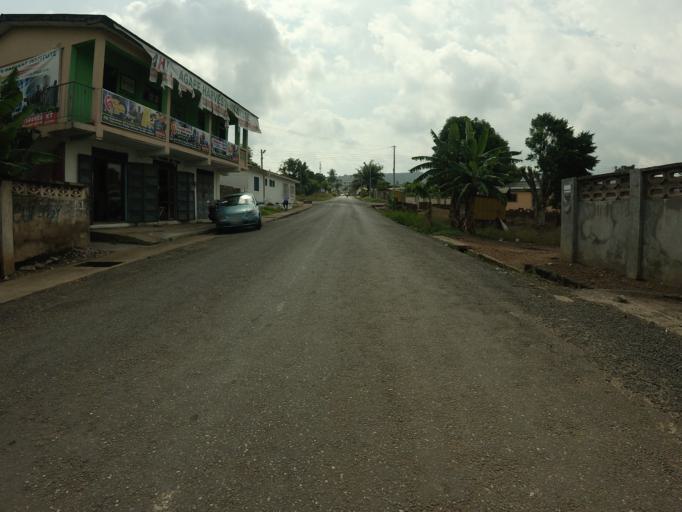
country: GH
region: Volta
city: Ho
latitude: 6.6164
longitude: 0.4772
